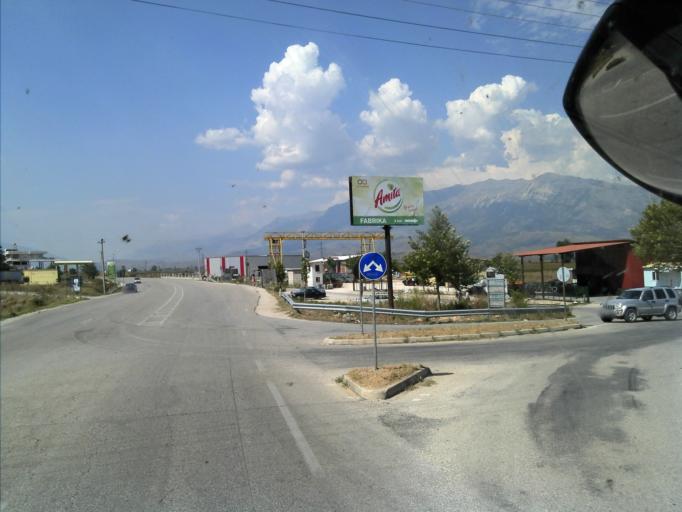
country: AL
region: Gjirokaster
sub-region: Rrethi i Gjirokastres
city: Dervician
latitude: 39.9973
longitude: 20.2160
